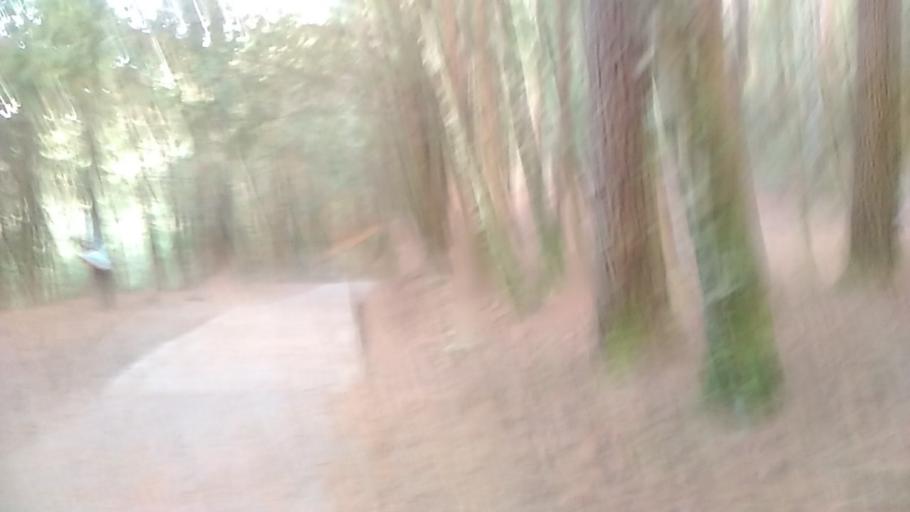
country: TW
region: Taiwan
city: Daxi
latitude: 24.4023
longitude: 121.3071
